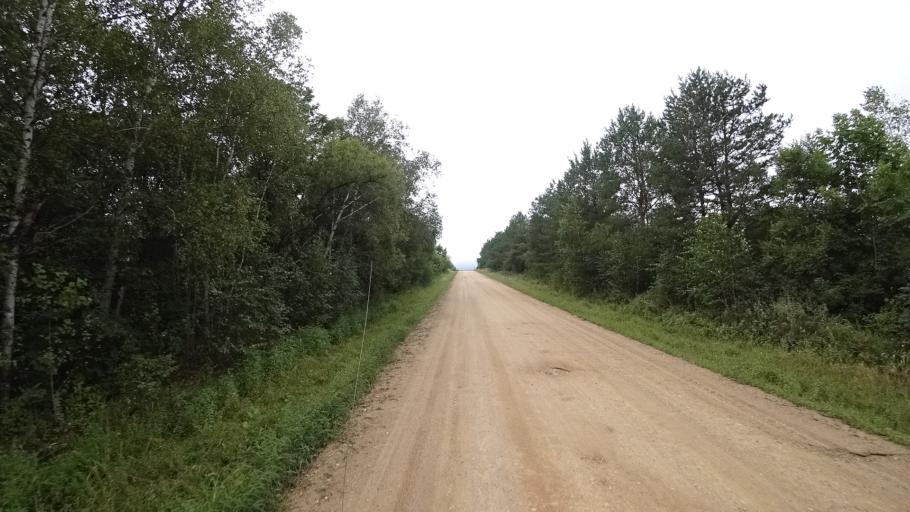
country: RU
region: Primorskiy
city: Monastyrishche
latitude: 44.0792
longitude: 132.5915
